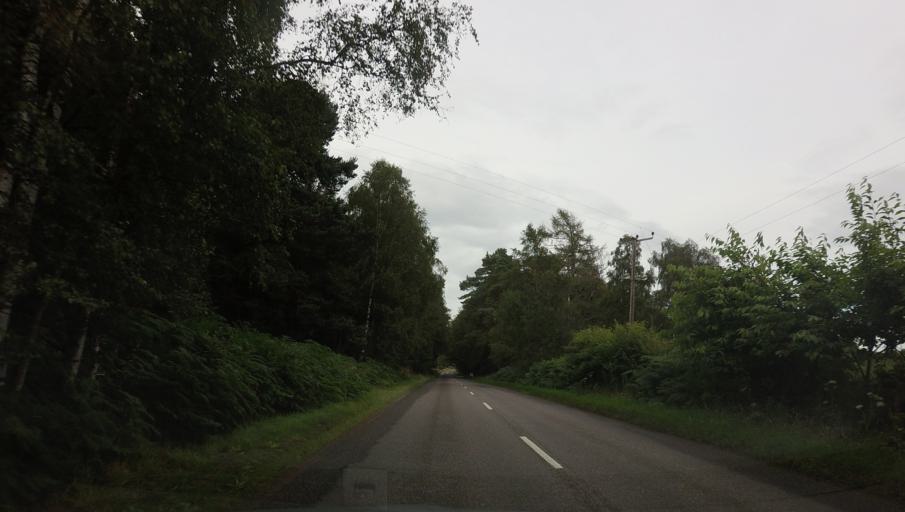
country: GB
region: Scotland
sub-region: Aberdeenshire
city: Torphins
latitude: 57.0593
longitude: -2.6204
